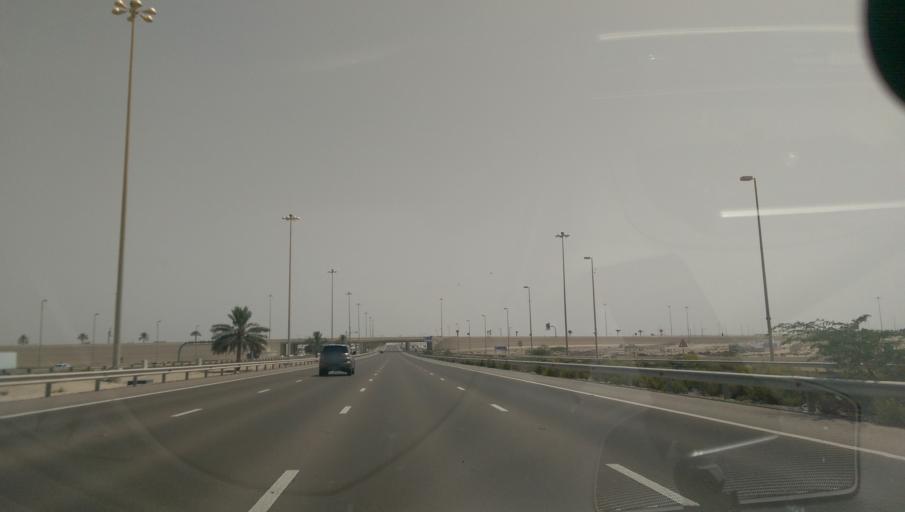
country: AE
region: Abu Dhabi
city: Abu Dhabi
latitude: 24.4054
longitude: 54.6714
